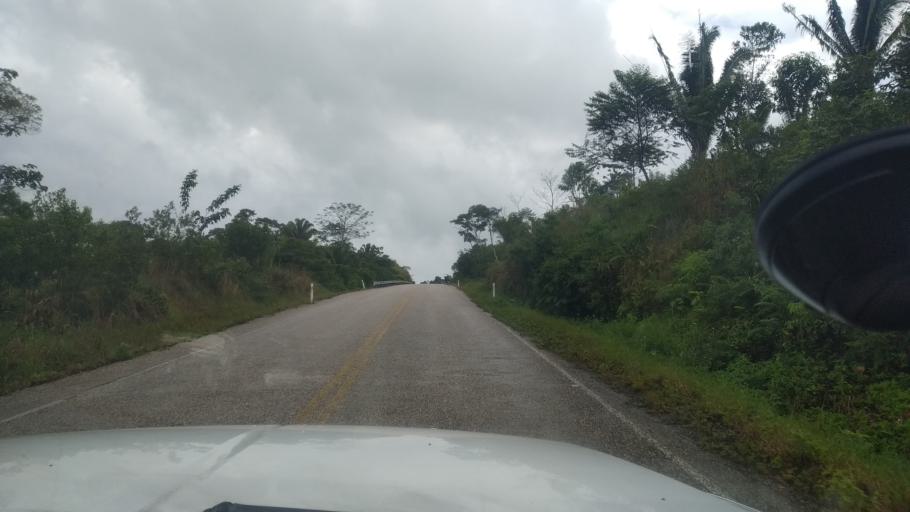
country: GT
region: Peten
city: San Luis
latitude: 16.1945
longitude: -89.1693
